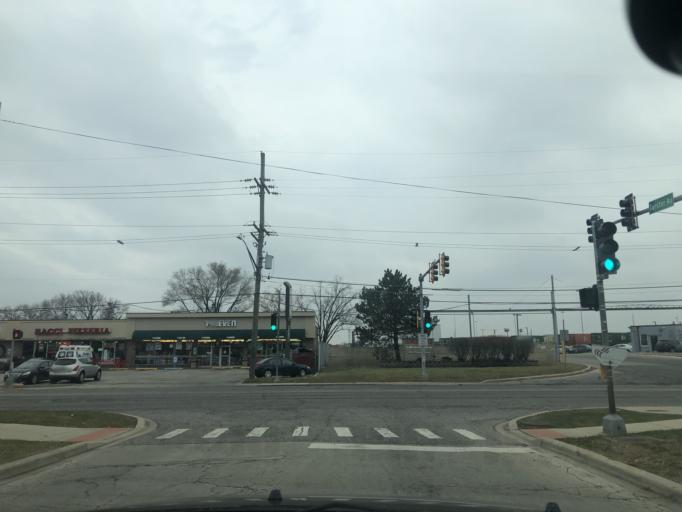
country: US
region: Illinois
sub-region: Cook County
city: Schiller Park
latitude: 41.9664
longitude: -87.8675
